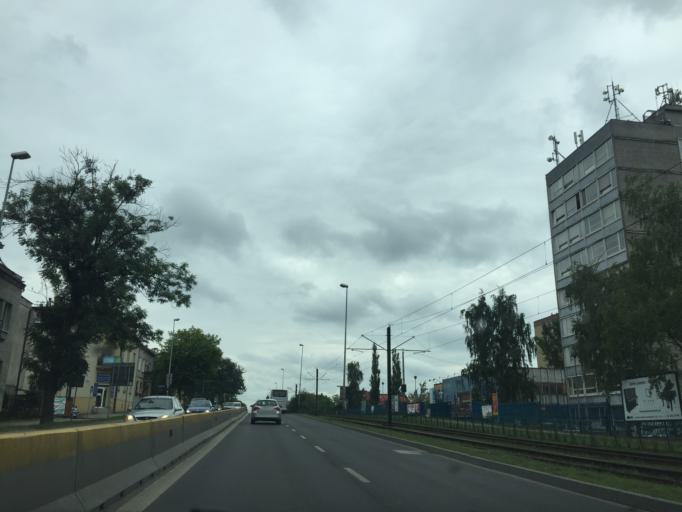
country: PL
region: Lesser Poland Voivodeship
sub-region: Krakow
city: Krakow
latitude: 50.0276
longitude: 19.9357
